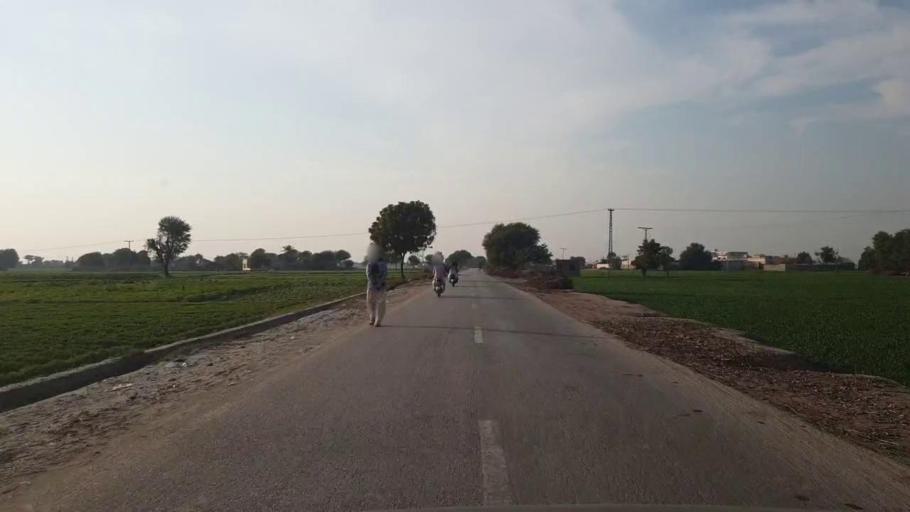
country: PK
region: Sindh
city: Shahpur Chakar
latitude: 26.1585
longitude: 68.6399
